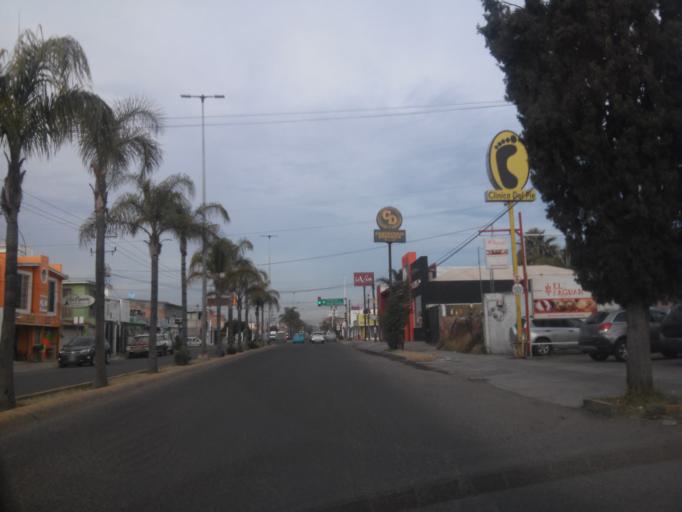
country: MX
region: Durango
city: Victoria de Durango
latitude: 24.0097
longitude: -104.6648
